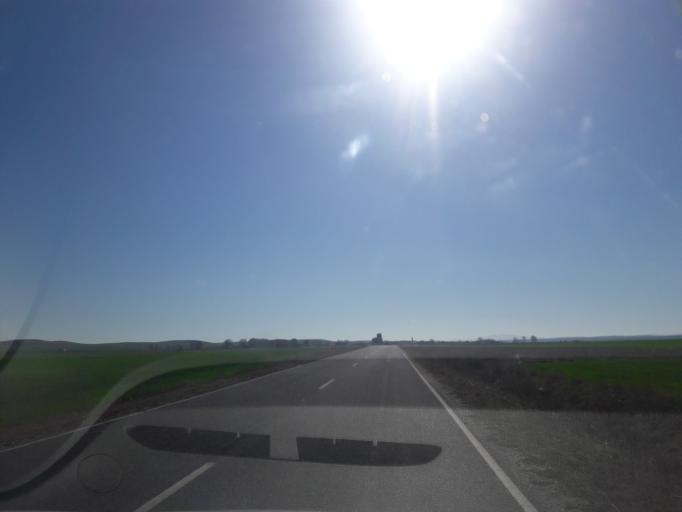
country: ES
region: Castille and Leon
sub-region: Provincia de Salamanca
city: Salmoral
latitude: 40.8075
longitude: -5.2353
